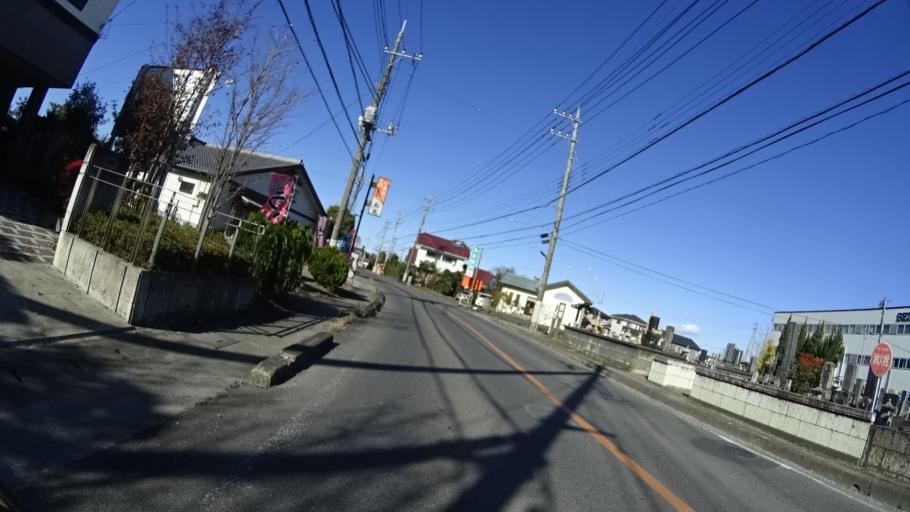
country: JP
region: Tochigi
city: Tochigi
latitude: 36.4233
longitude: 139.7498
